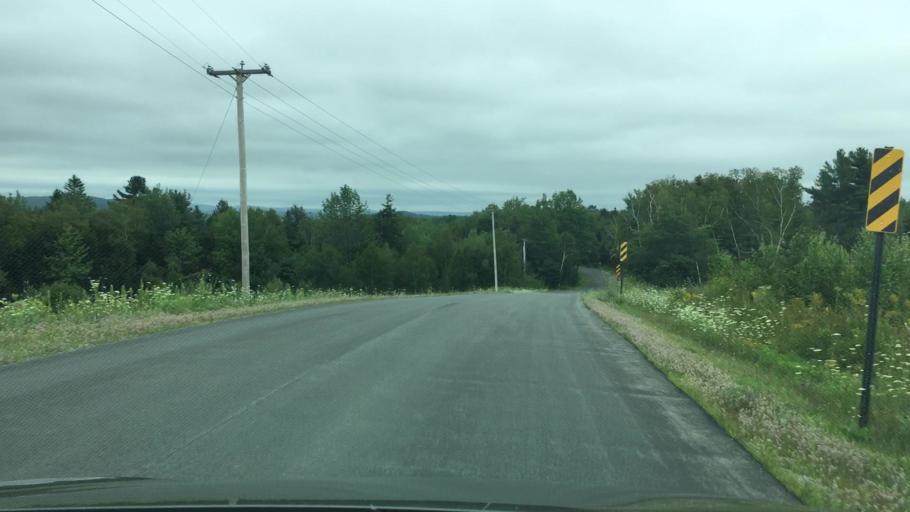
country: US
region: Maine
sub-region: Waldo County
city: Stockton Springs
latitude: 44.5261
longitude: -68.8788
